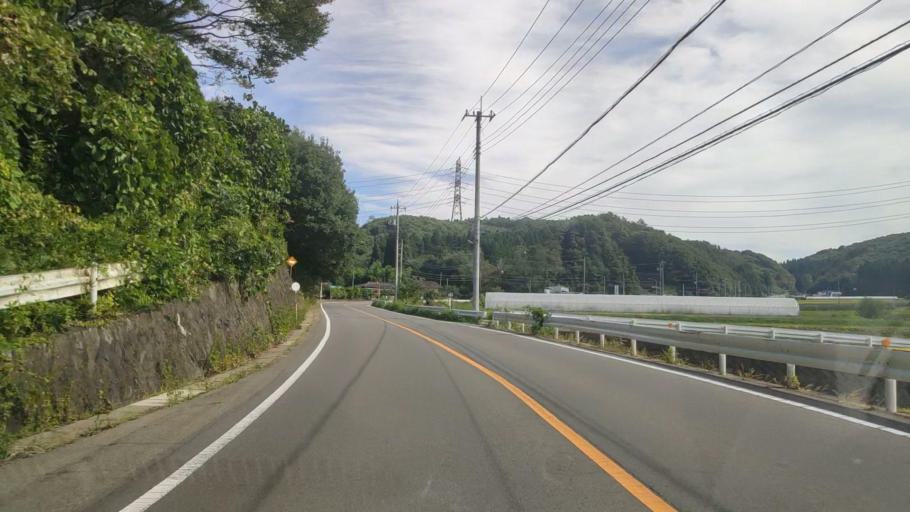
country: JP
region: Gunma
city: Numata
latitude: 36.6285
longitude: 138.9741
